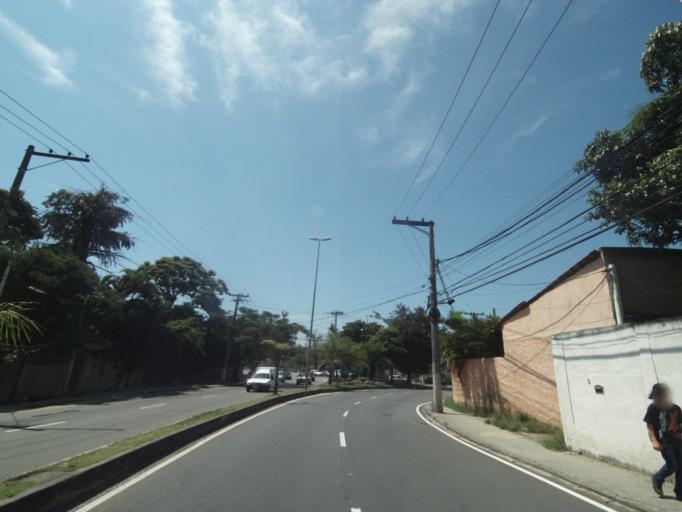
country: BR
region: Rio de Janeiro
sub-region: Sao Goncalo
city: Sao Goncalo
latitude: -22.8792
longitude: -43.0270
